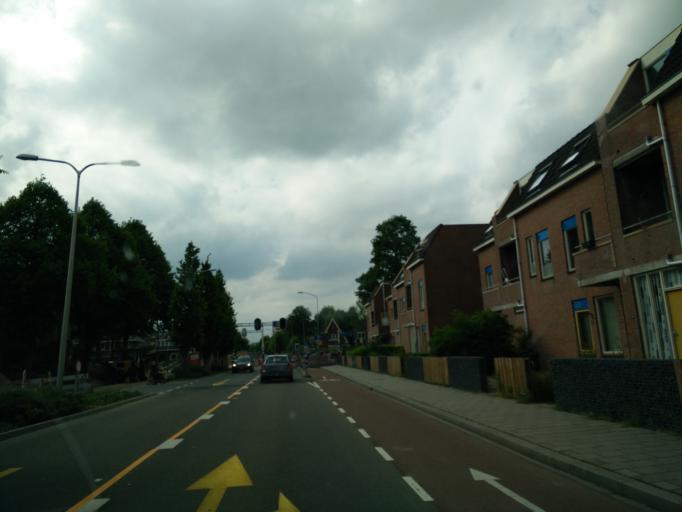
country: NL
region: Drenthe
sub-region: Gemeente Assen
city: Assen
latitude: 52.9964
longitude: 6.5568
